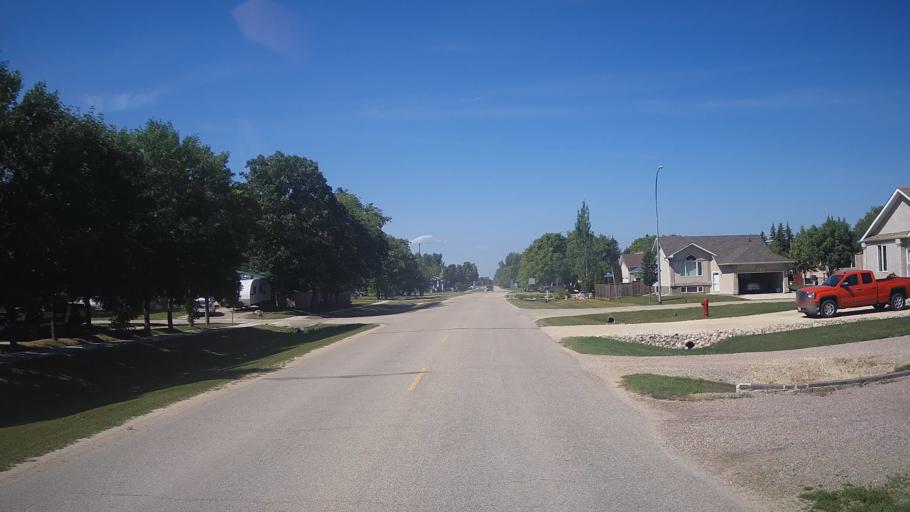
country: CA
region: Manitoba
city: Stonewall
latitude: 50.1284
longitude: -97.3333
